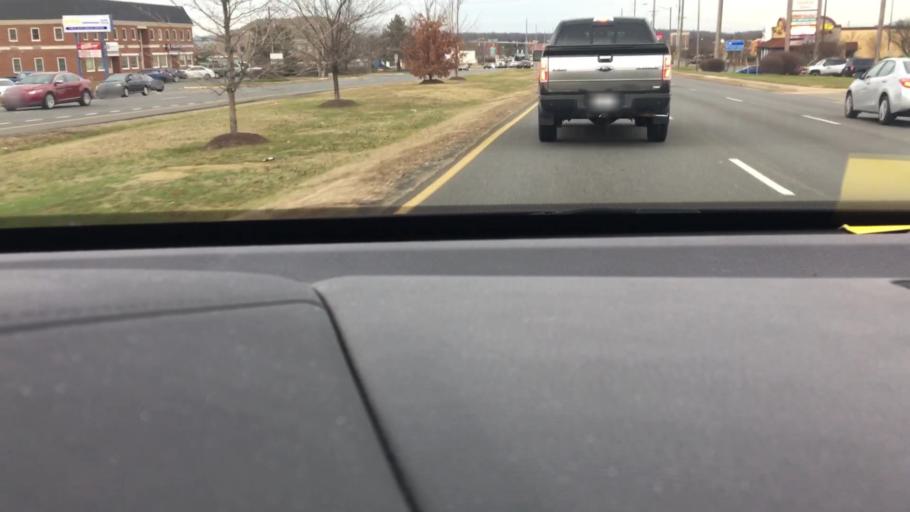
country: US
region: Virginia
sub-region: Prince William County
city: Bull Run
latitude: 38.7856
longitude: -77.5131
